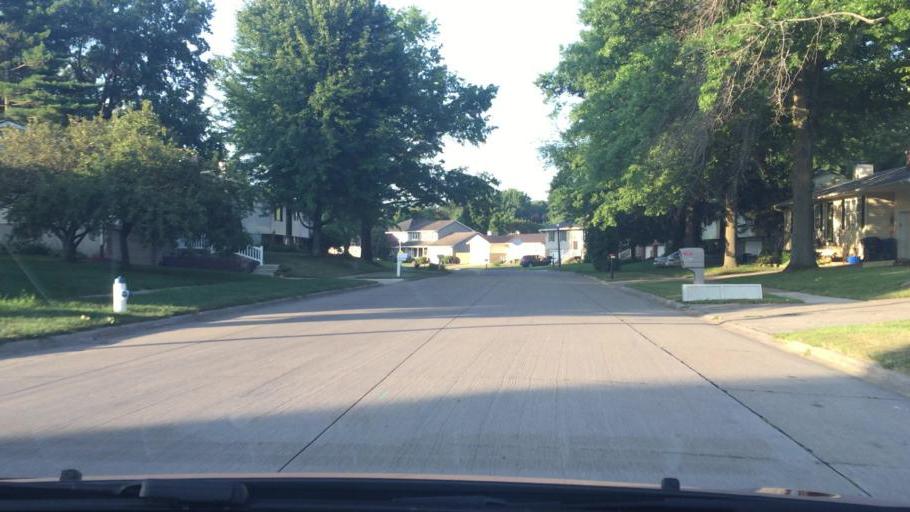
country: US
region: Iowa
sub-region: Muscatine County
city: Muscatine
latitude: 41.4427
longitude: -91.0555
